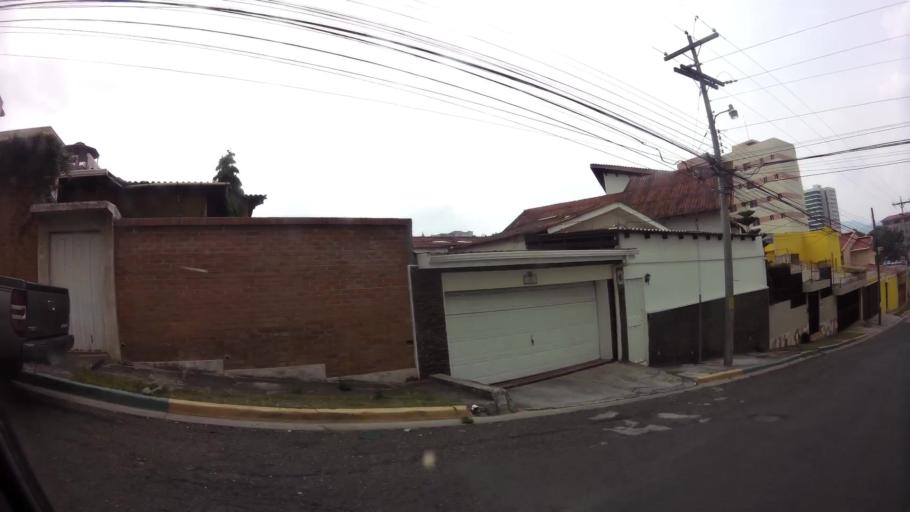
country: HN
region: Francisco Morazan
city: Tegucigalpa
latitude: 14.0918
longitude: -87.1795
